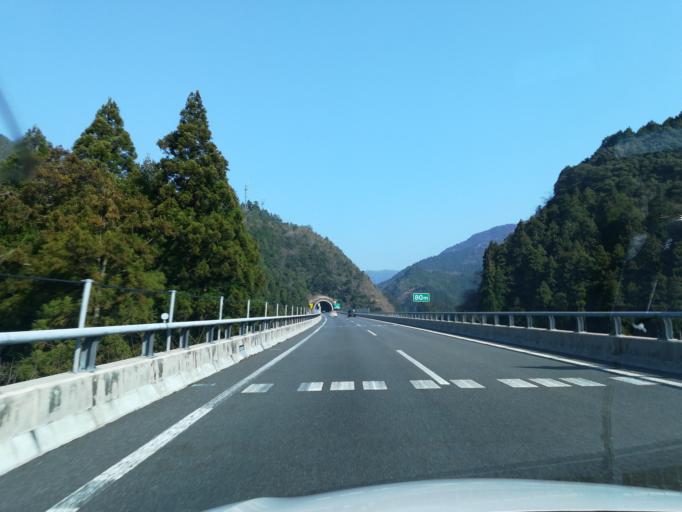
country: JP
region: Ehime
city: Kawanoecho
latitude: 33.8233
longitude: 133.6625
